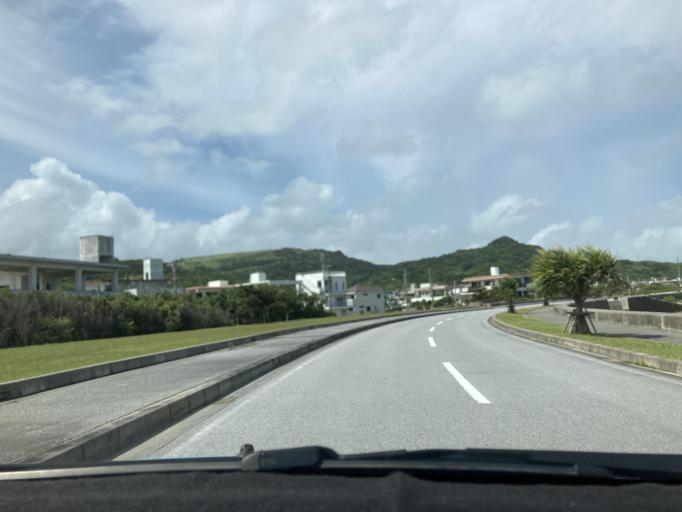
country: JP
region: Okinawa
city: Ginowan
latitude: 26.1796
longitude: 127.8232
